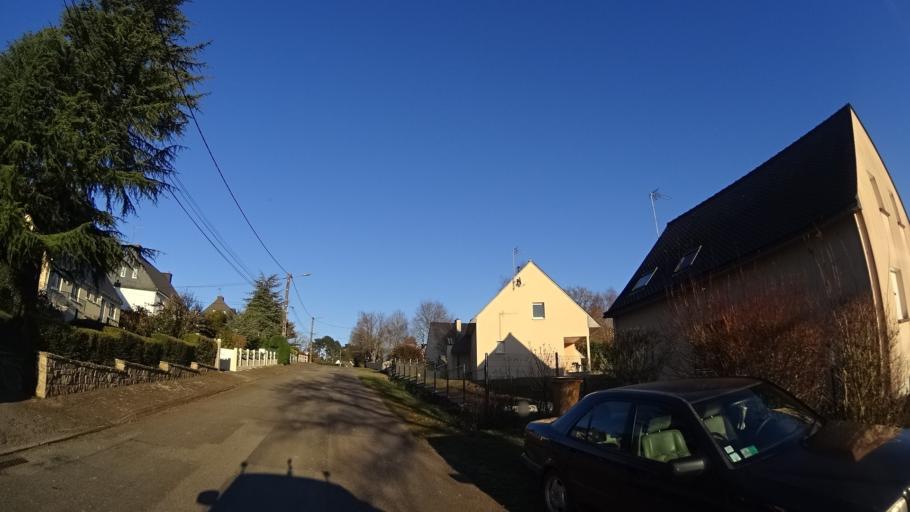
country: FR
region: Brittany
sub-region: Departement du Morbihan
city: Saint-Jean-la-Poterie
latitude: 47.6326
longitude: -2.1187
